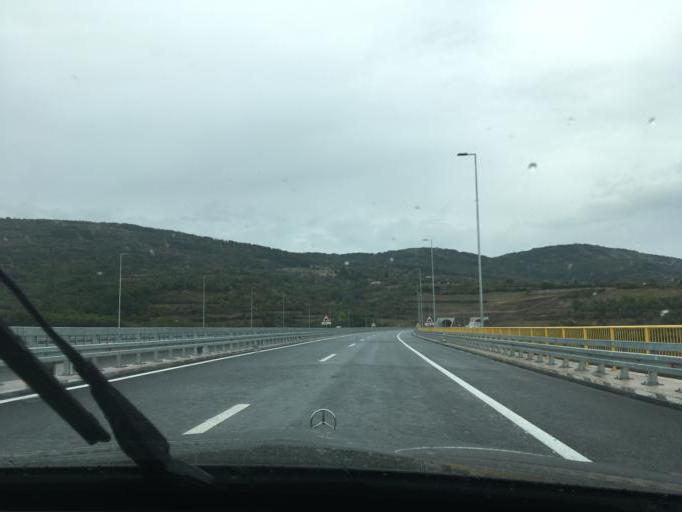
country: RS
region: Central Serbia
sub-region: Pirotski Okrug
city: Dimitrovgrad
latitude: 43.0234
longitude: 22.7767
